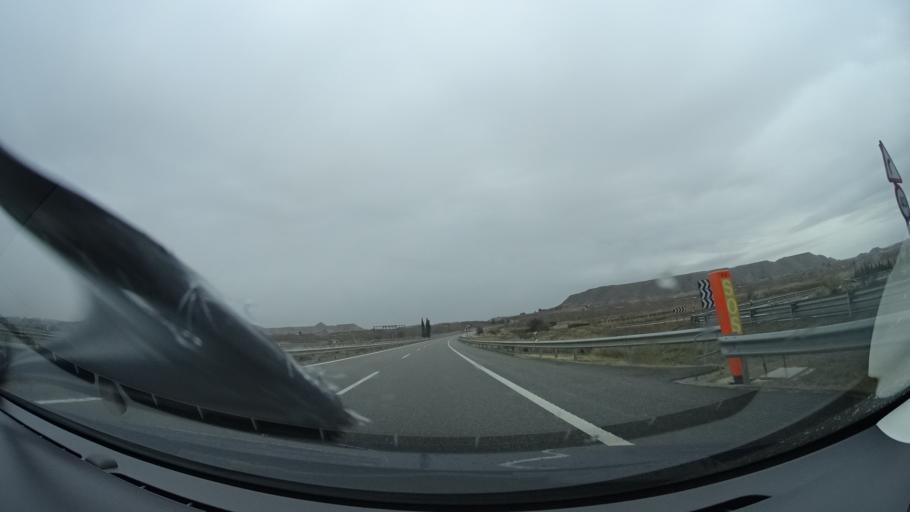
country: ES
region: Aragon
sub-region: Provincia de Huesca
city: Fraga
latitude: 41.4898
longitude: 0.3397
